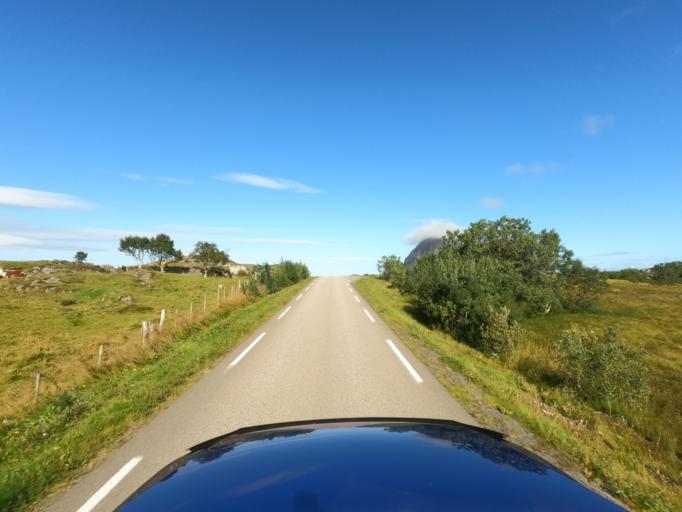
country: NO
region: Nordland
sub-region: Vestvagoy
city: Evjen
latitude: 68.3072
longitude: 14.0979
